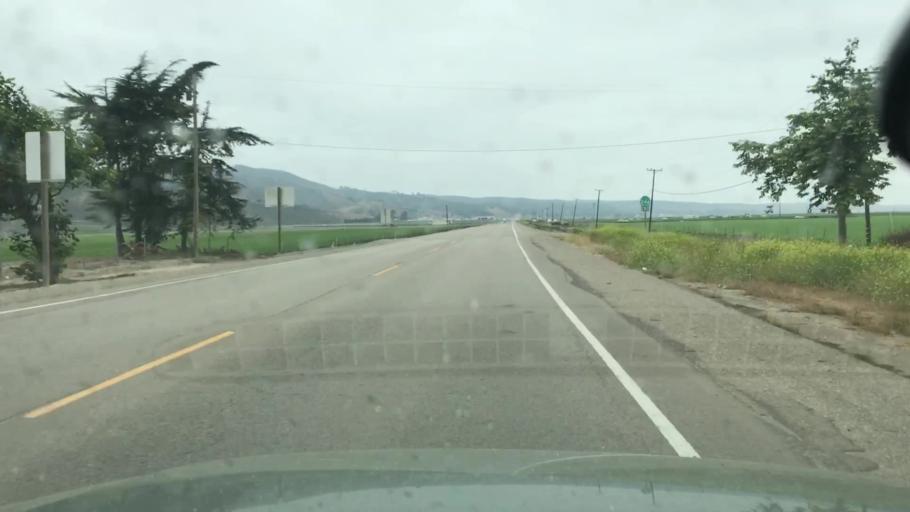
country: US
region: California
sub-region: Santa Barbara County
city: Lompoc
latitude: 34.6392
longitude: -120.4790
